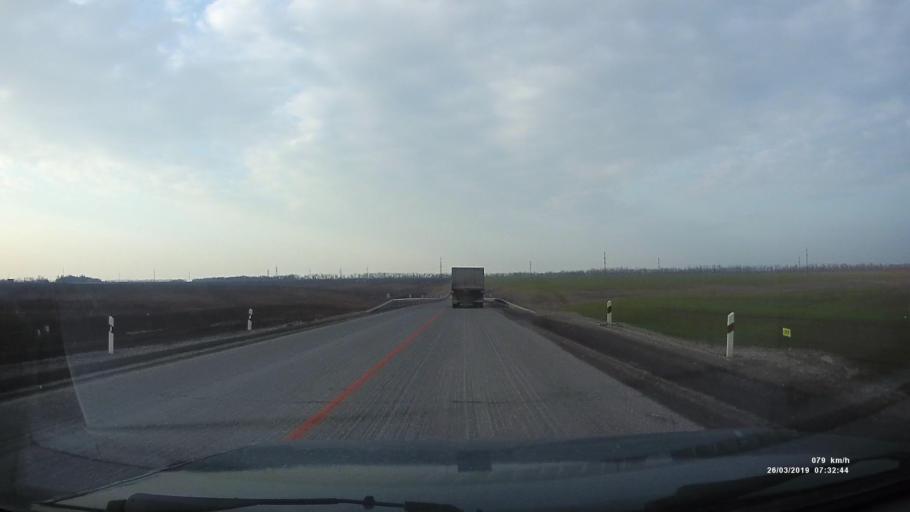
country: RU
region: Rostov
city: Novobessergenovka
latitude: 47.2225
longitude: 38.7755
